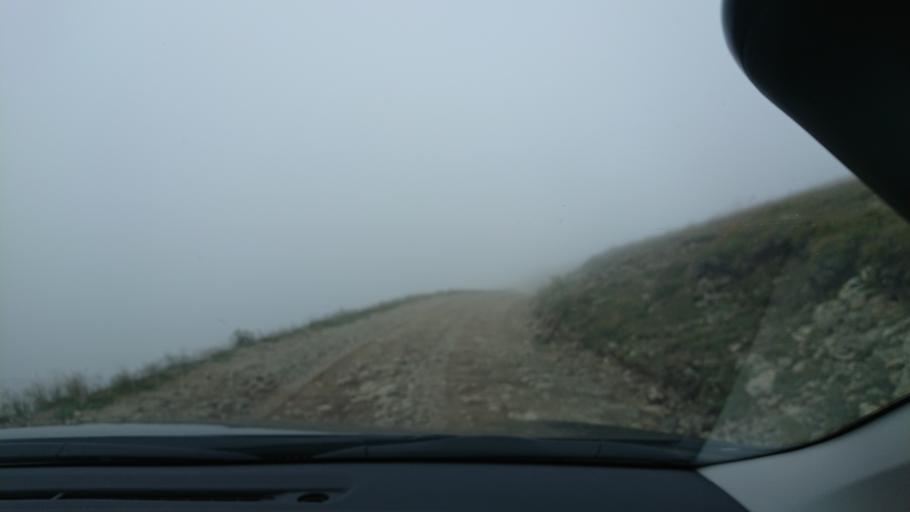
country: TR
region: Gumushane
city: Kurtun
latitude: 40.6257
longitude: 38.9936
